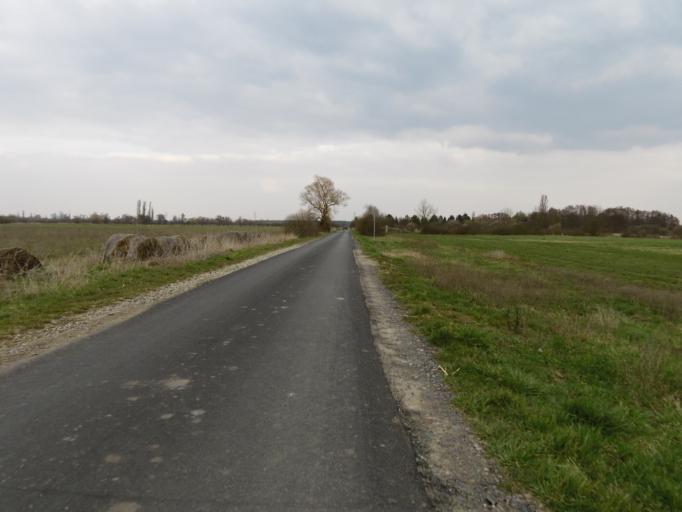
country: DE
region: Rheinland-Pfalz
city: Erpolzheim
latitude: 49.4794
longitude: 8.2348
